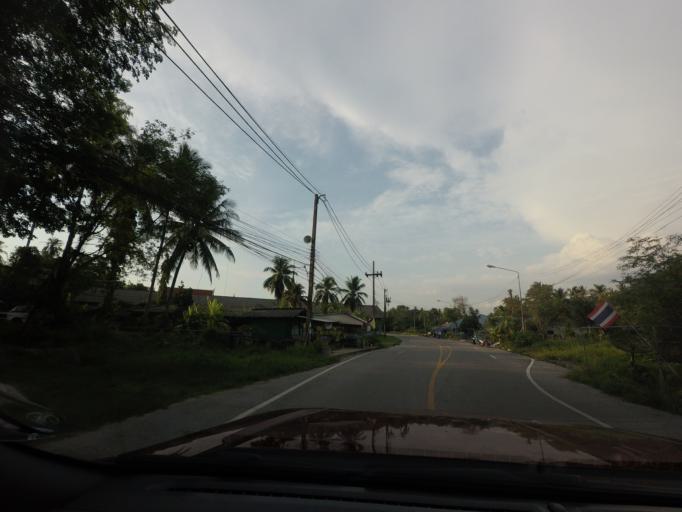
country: TH
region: Pattani
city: Khok Pho
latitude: 6.6717
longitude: 101.1051
